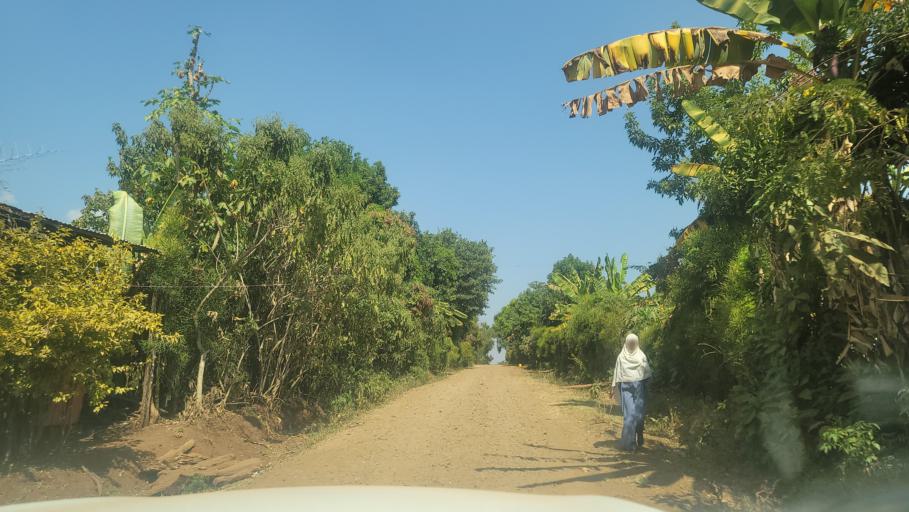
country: ET
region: Oromiya
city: Agaro
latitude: 7.8492
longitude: 36.5390
